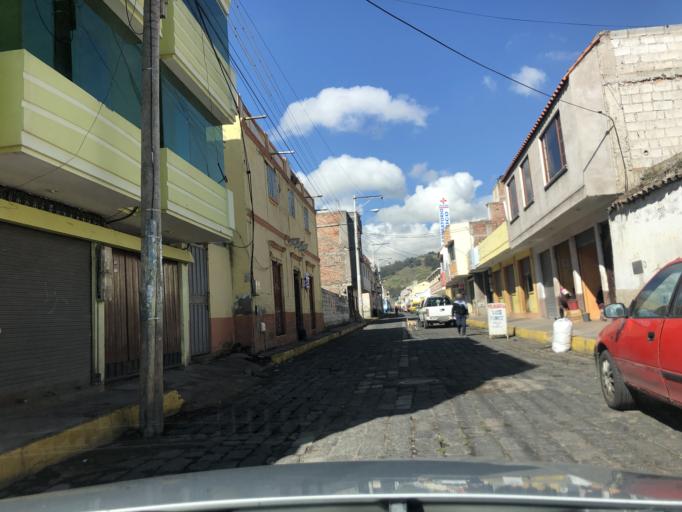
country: EC
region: Chimborazo
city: Riobamba
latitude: -1.7007
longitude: -78.7721
